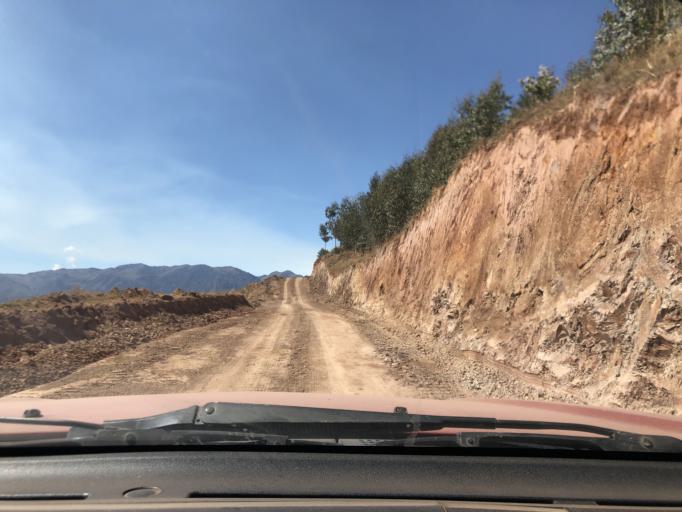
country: PE
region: Ayacucho
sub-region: Provincia de La Mar
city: Chilcas
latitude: -13.1816
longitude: -73.8417
